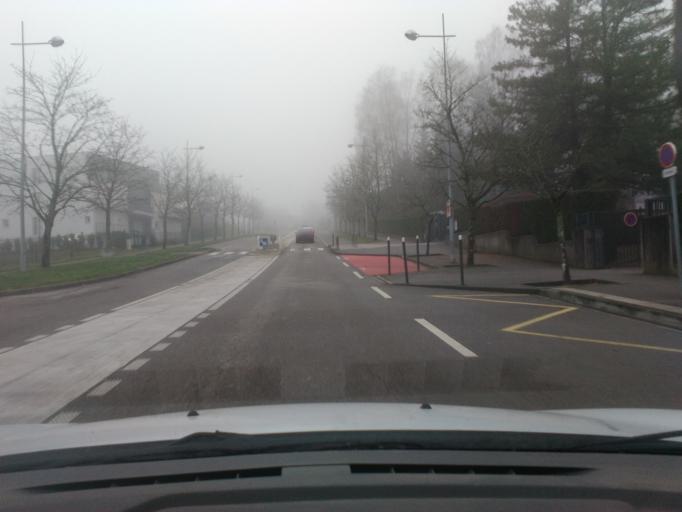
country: FR
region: Lorraine
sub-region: Departement des Vosges
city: Epinal
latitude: 48.1891
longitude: 6.4624
